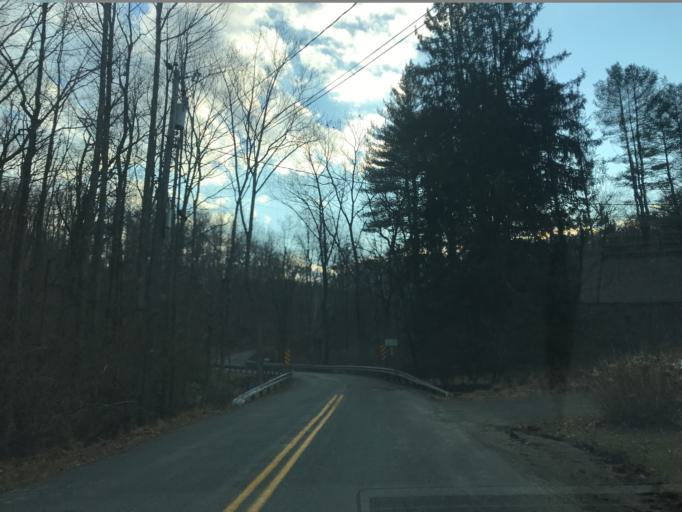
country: US
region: Maryland
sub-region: Harford County
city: Jarrettsville
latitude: 39.6311
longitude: -76.4157
